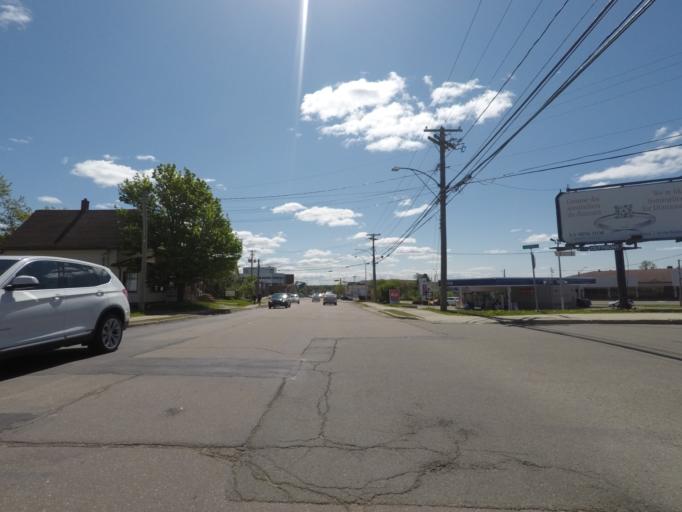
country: CA
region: New Brunswick
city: Moncton
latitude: 46.0958
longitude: -64.7519
